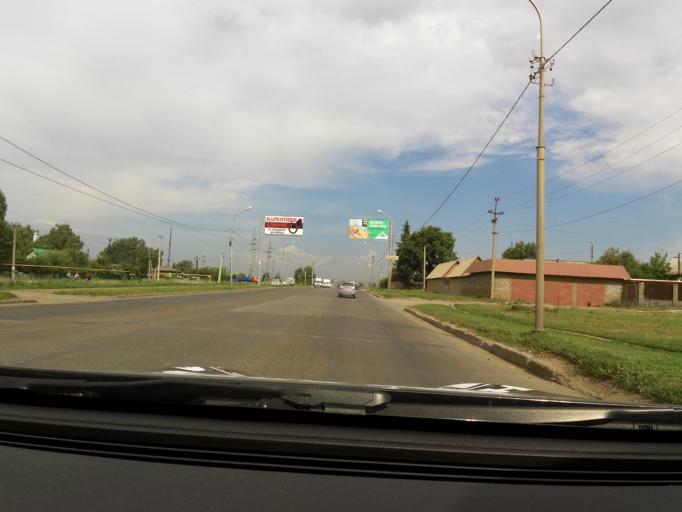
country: RU
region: Bashkortostan
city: Iglino
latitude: 54.7794
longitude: 56.2281
